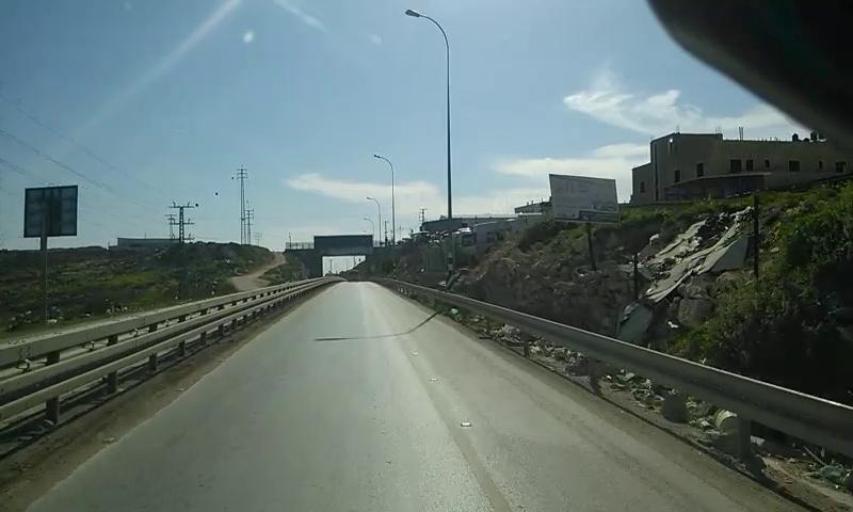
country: PS
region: West Bank
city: Ar Ram wa Dahiyat al Barid
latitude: 31.8546
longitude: 35.2451
